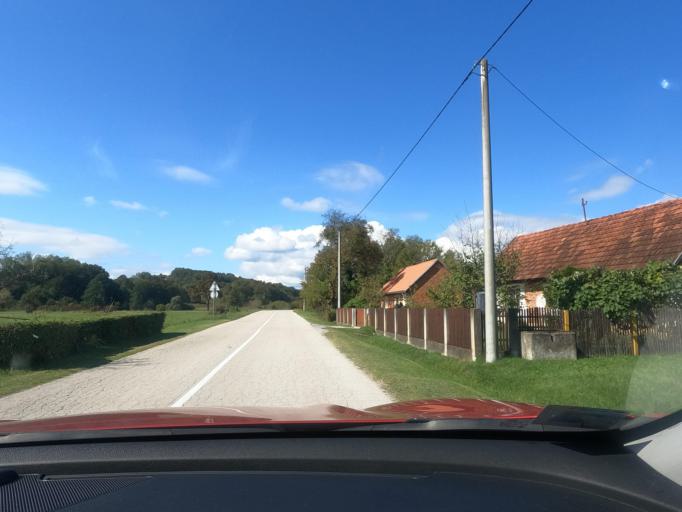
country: BA
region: Federation of Bosnia and Herzegovina
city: Podzvizd
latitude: 45.2270
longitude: 15.9091
